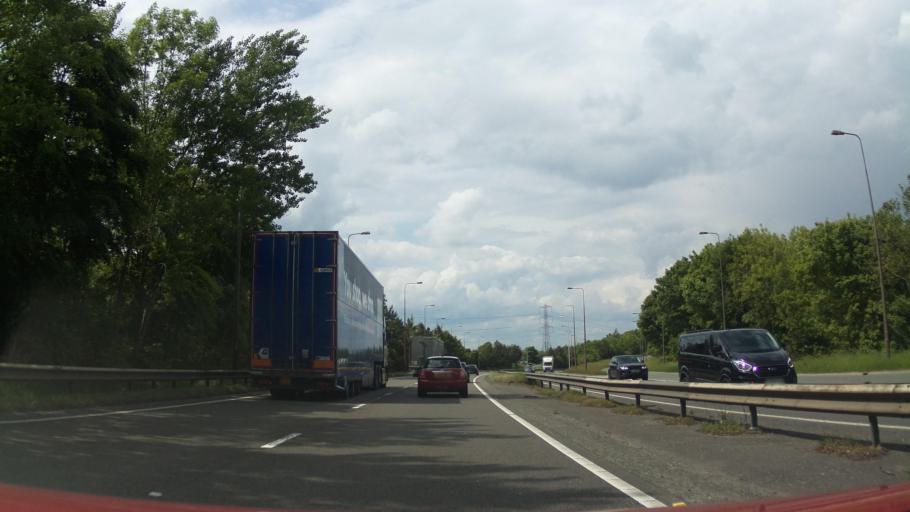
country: GB
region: England
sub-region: County Durham
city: Wingate
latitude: 54.7347
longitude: -1.3584
